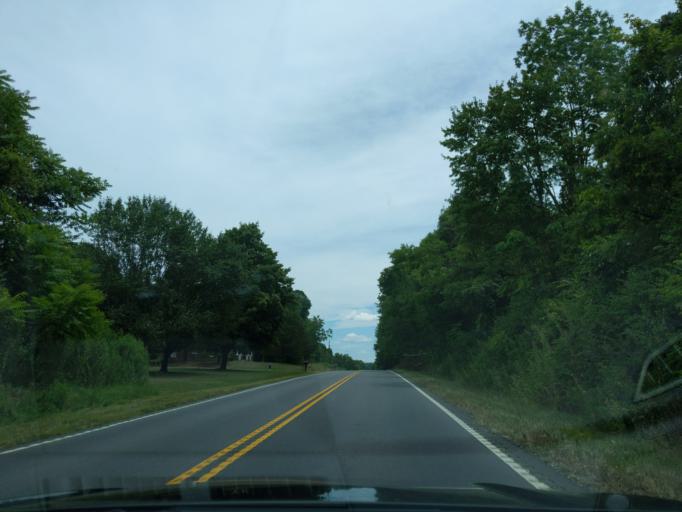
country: US
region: North Carolina
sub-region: Cabarrus County
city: Mount Pleasant
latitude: 35.4375
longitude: -80.3813
